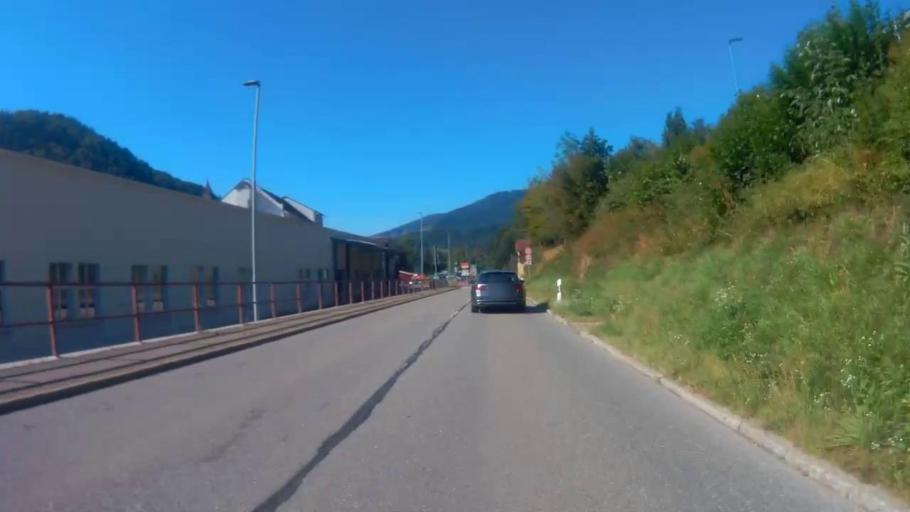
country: DE
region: Baden-Wuerttemberg
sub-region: Freiburg Region
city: Schonau im Schwarzwald
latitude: 47.7785
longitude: 7.8934
